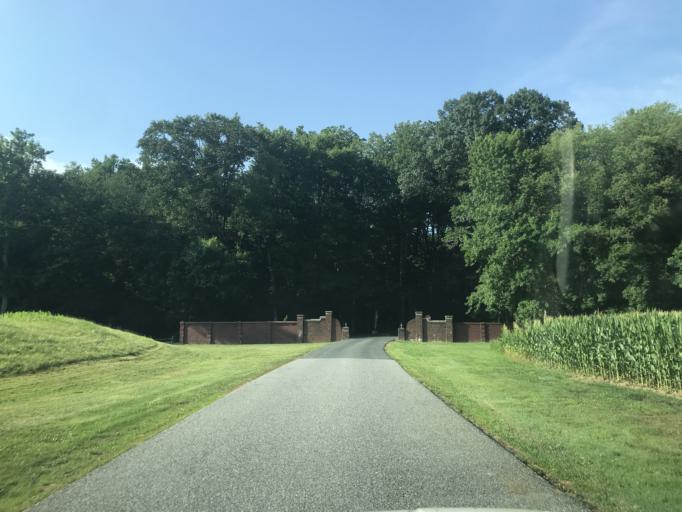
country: US
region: Maryland
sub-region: Harford County
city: Aberdeen
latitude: 39.5124
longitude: -76.1254
